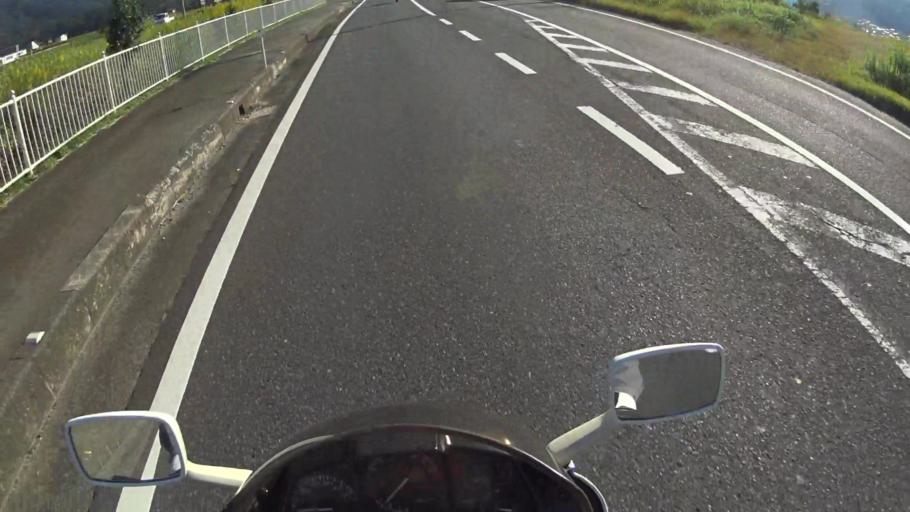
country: JP
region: Kyoto
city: Miyazu
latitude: 35.5041
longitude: 135.1038
